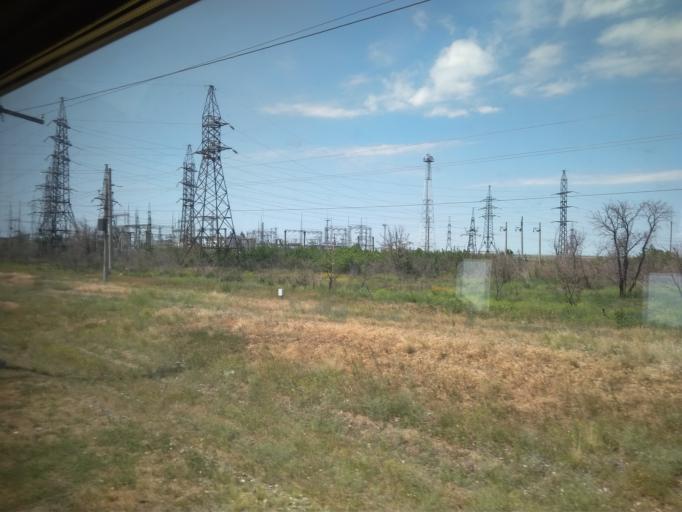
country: RU
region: Volgograd
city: Gumrak
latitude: 48.7602
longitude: 44.4259
